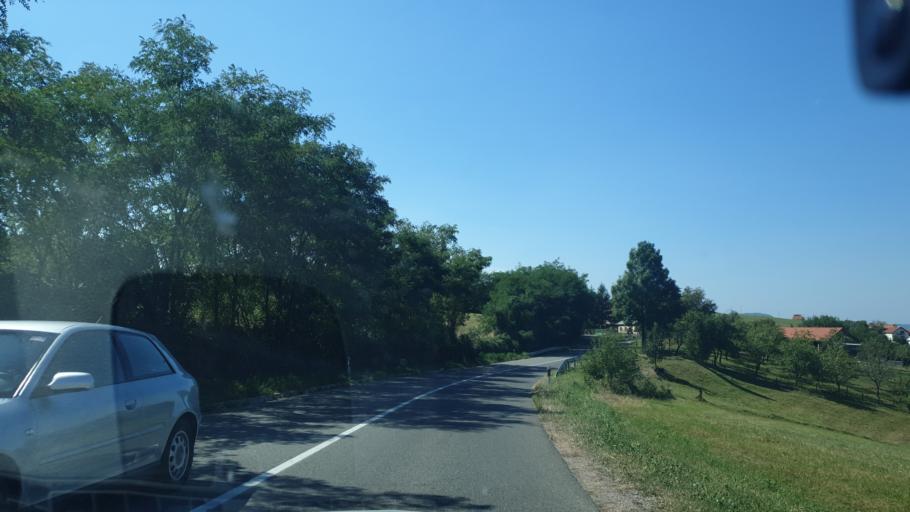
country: RS
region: Central Serbia
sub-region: Kolubarski Okrug
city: Mionica
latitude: 44.1761
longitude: 20.0286
